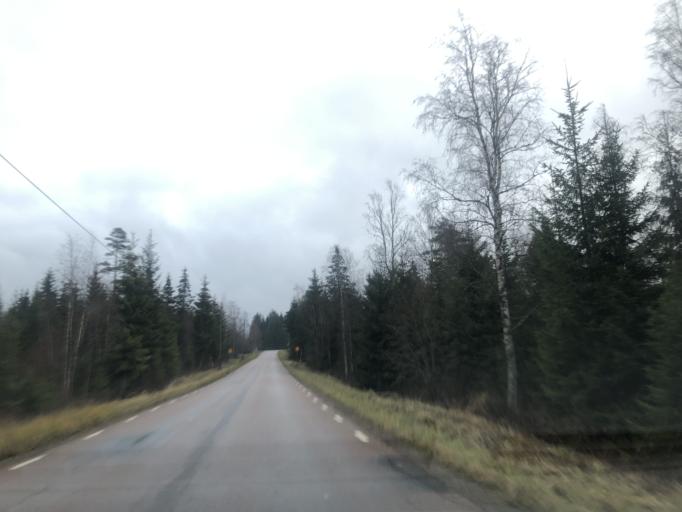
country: SE
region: Vaestra Goetaland
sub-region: Ulricehamns Kommun
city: Ulricehamn
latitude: 57.8259
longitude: 13.5133
